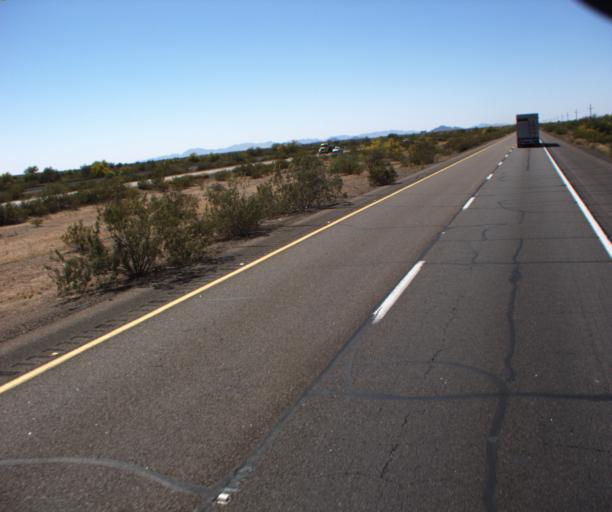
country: US
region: Arizona
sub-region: Maricopa County
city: Gila Bend
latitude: 32.8455
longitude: -113.2824
